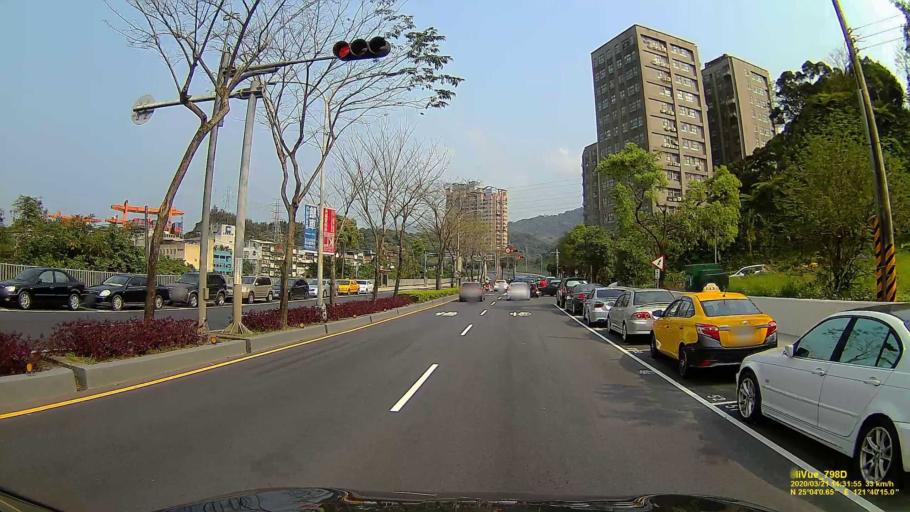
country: TW
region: Taiwan
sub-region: Keelung
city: Keelung
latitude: 25.0668
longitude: 121.6704
